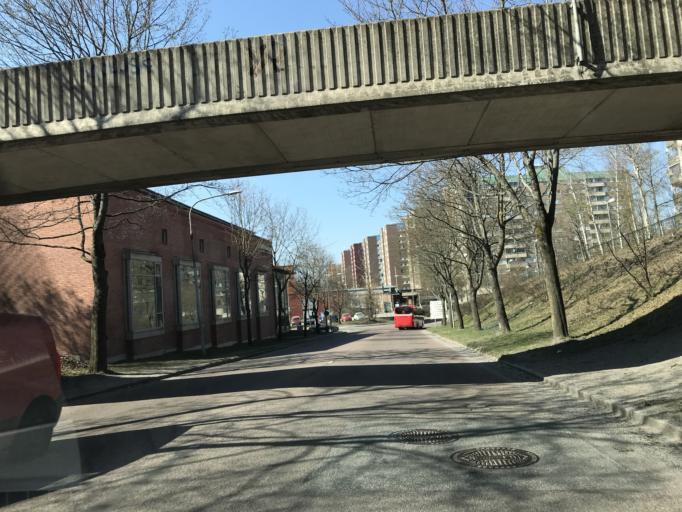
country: SE
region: Stockholm
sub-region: Stockholms Kommun
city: Kista
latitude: 59.4118
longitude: 17.9241
